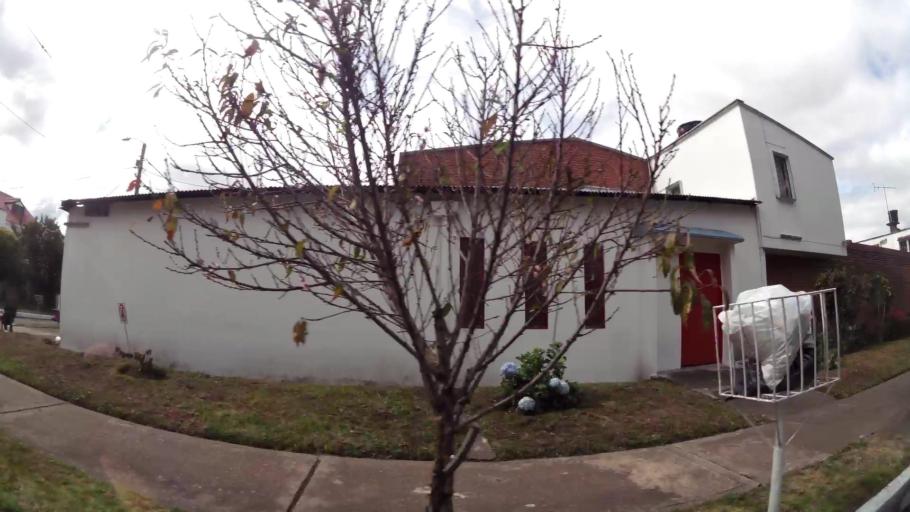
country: CO
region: Bogota D.C.
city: Barrio San Luis
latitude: 4.6916
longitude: -74.0640
